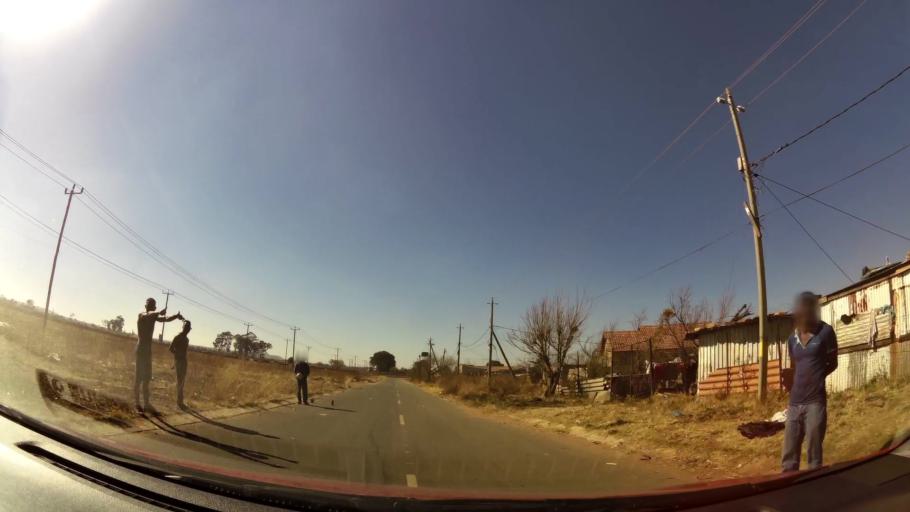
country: ZA
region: Gauteng
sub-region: City of Johannesburg Metropolitan Municipality
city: Soweto
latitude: -26.2157
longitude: 27.8381
